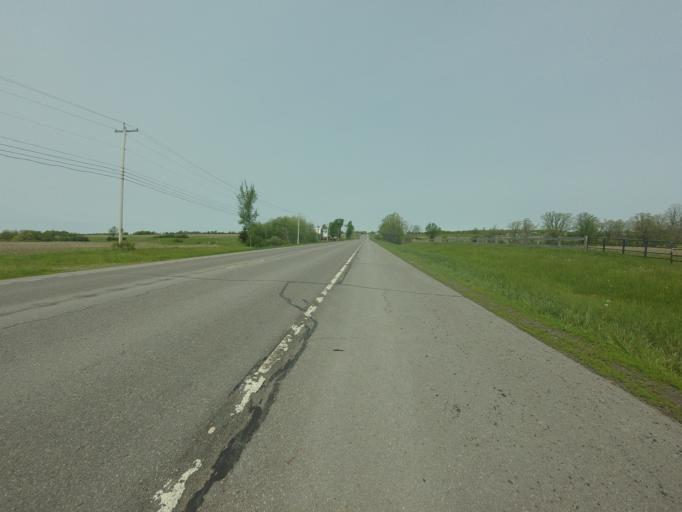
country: US
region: New York
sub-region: Jefferson County
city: Dexter
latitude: 44.0518
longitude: -76.1014
